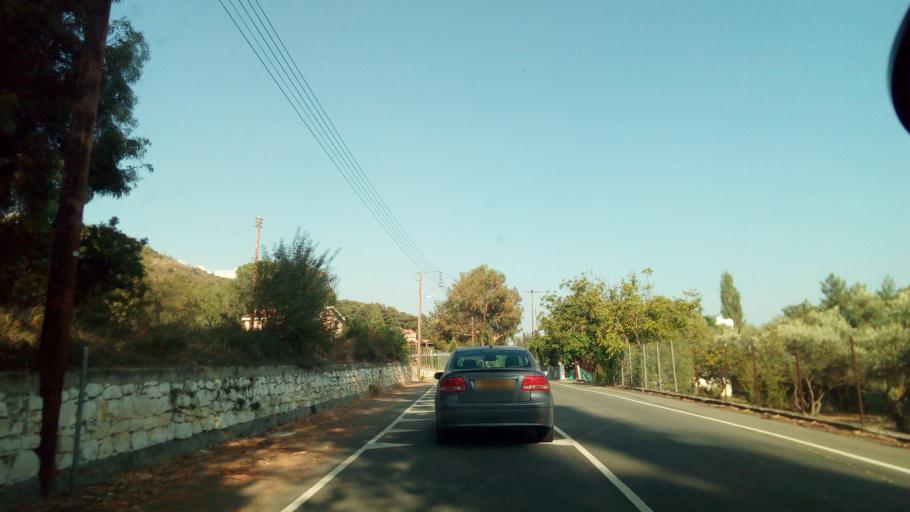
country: CY
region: Limassol
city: Pelendri
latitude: 34.8620
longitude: 32.8686
